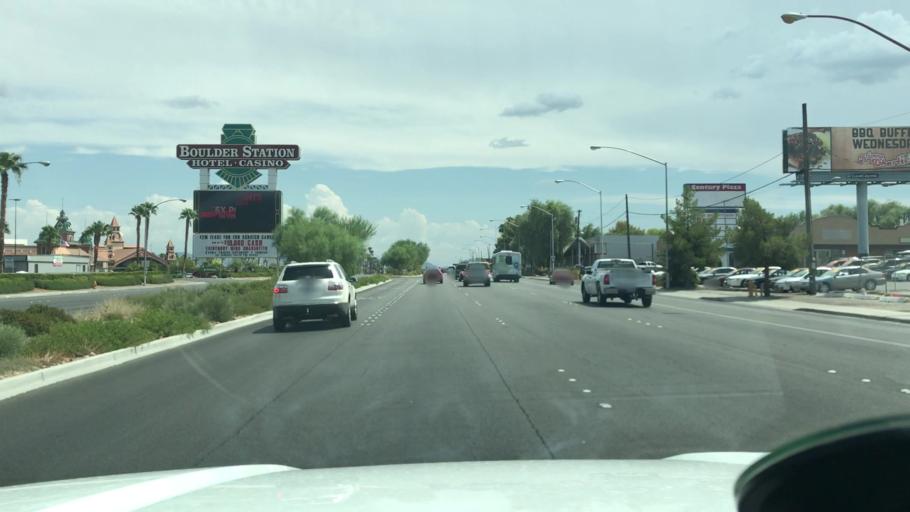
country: US
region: Nevada
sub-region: Clark County
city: Winchester
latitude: 36.1341
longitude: -115.0885
